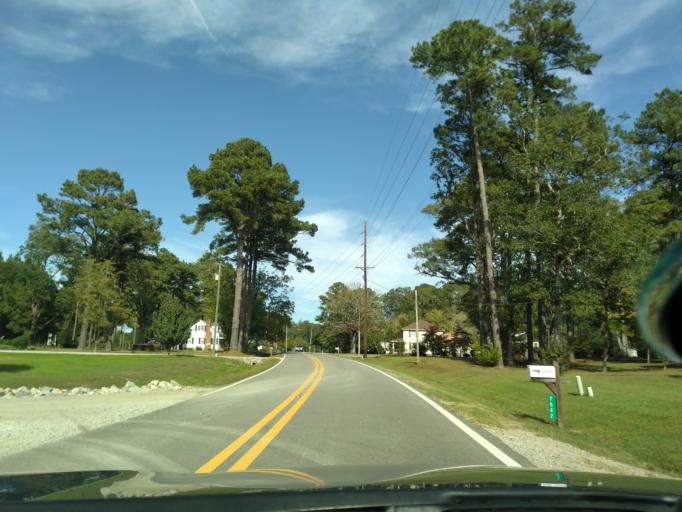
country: US
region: North Carolina
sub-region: Beaufort County
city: River Road
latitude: 35.5204
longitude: -76.9577
